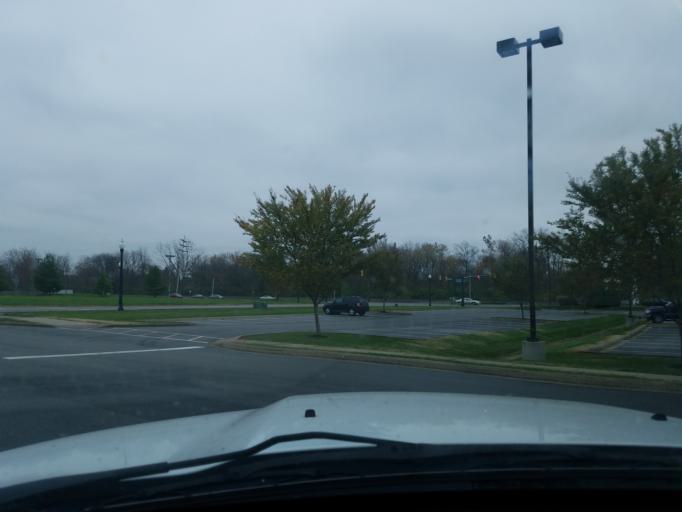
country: US
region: Indiana
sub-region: Clark County
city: Clarksville
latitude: 38.3224
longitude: -85.7494
